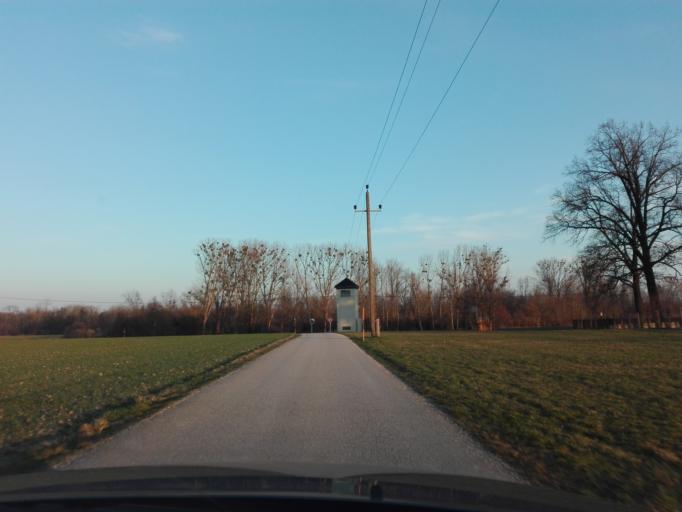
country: AT
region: Upper Austria
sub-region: Politischer Bezirk Urfahr-Umgebung
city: Feldkirchen an der Donau
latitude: 48.3512
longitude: 14.0093
